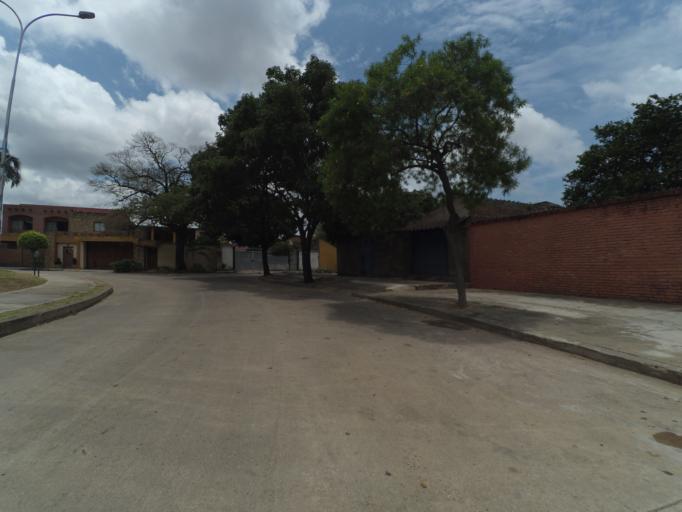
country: BO
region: Santa Cruz
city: Santa Cruz de la Sierra
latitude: -17.8019
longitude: -63.1993
